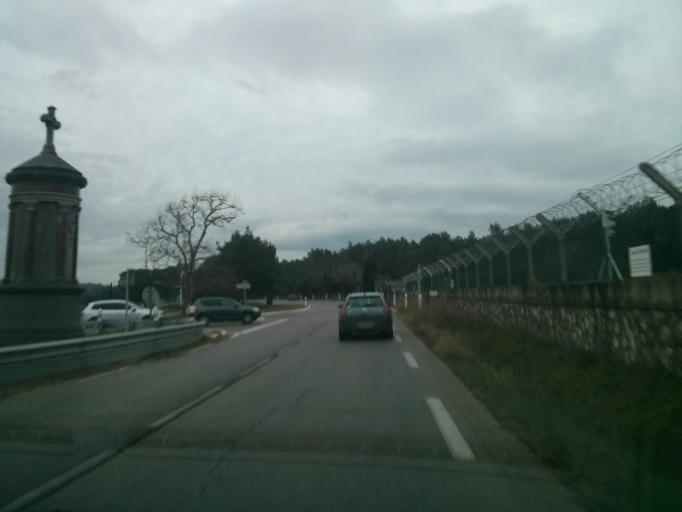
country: FR
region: Provence-Alpes-Cote d'Azur
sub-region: Departement des Bouches-du-Rhone
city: Fontvieille
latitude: 43.7289
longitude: 4.7368
